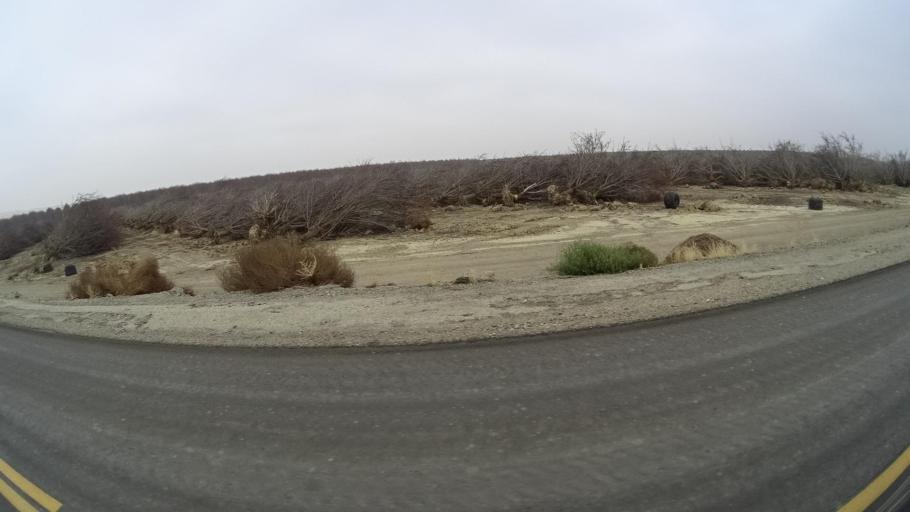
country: US
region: California
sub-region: Kern County
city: Maricopa
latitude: 35.1172
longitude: -119.3557
